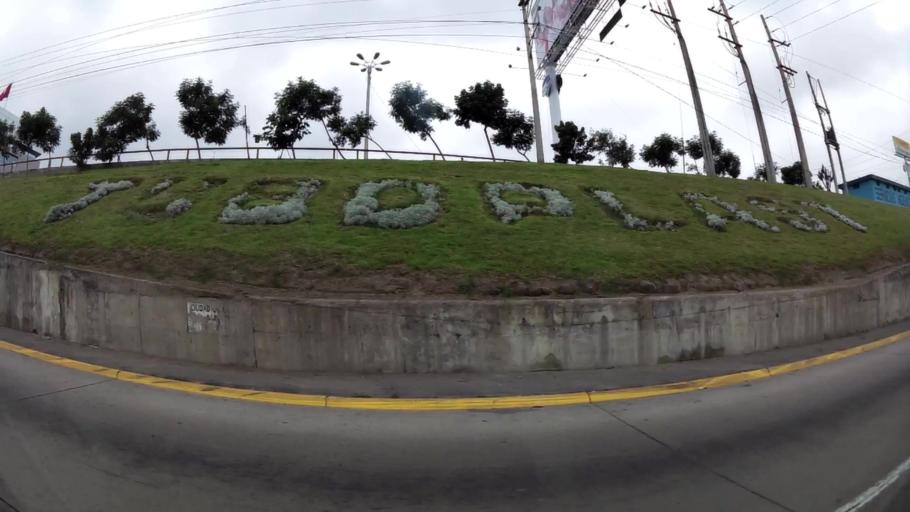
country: PE
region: Lima
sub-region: Lima
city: San Isidro
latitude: -12.1128
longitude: -77.0259
